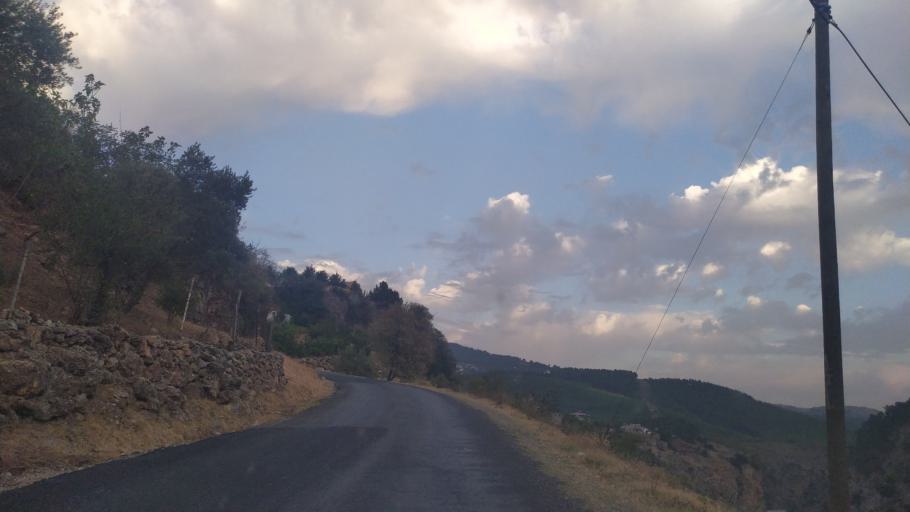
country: TR
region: Mersin
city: Camliyayla
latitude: 37.2386
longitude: 34.7170
